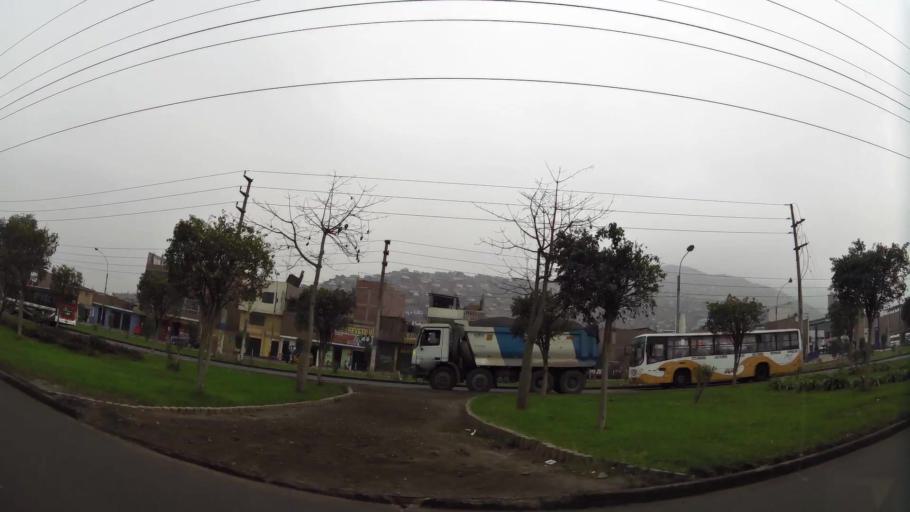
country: PE
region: Lima
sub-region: Lima
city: Urb. Santo Domingo
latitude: -11.9351
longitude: -76.9700
